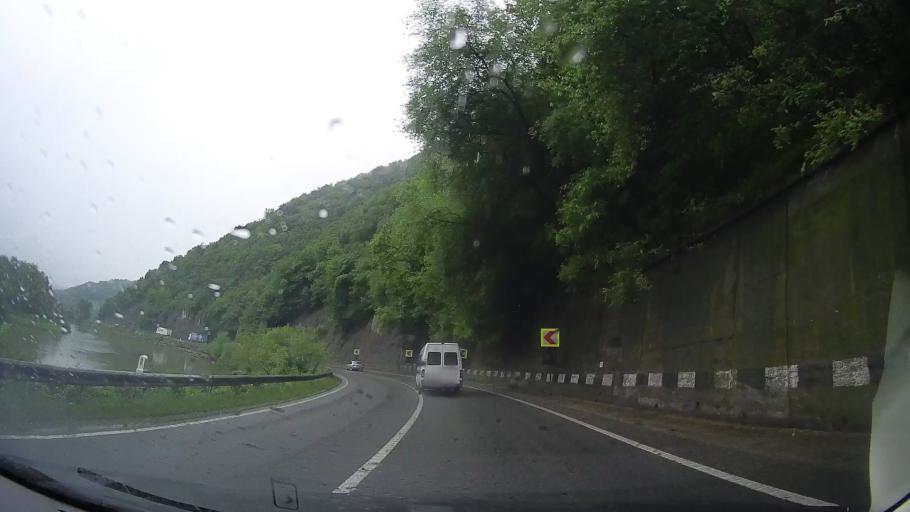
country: RO
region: Mehedinti
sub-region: Municipiul Orsova
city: Orsova
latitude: 44.7505
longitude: 22.3916
